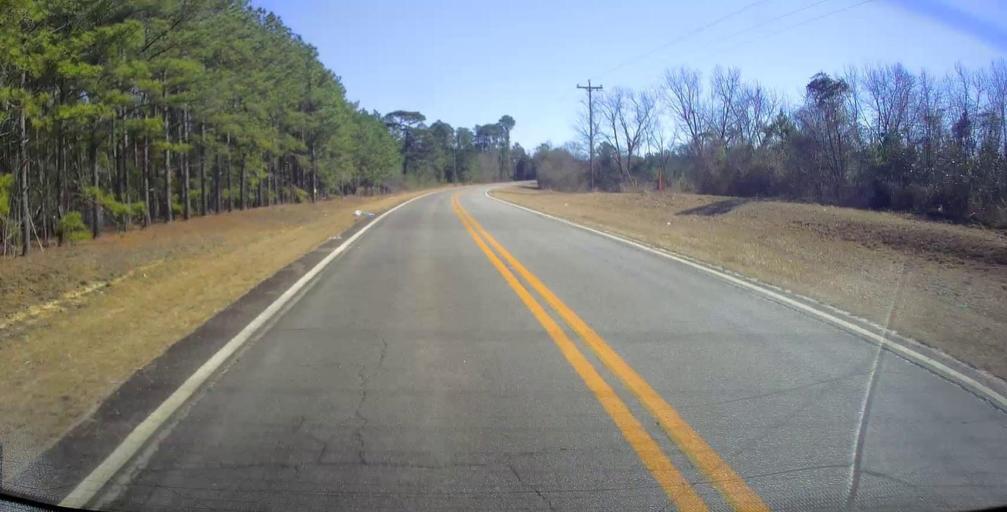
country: US
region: Georgia
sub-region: Crawford County
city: Roberta
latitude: 32.6310
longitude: -83.9915
